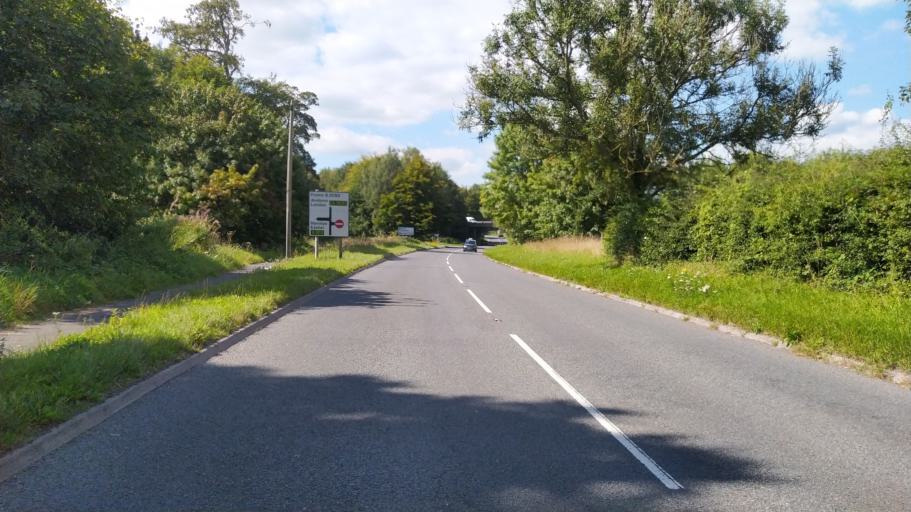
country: GB
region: England
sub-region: Wiltshire
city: Mere
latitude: 51.0896
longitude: -2.2918
